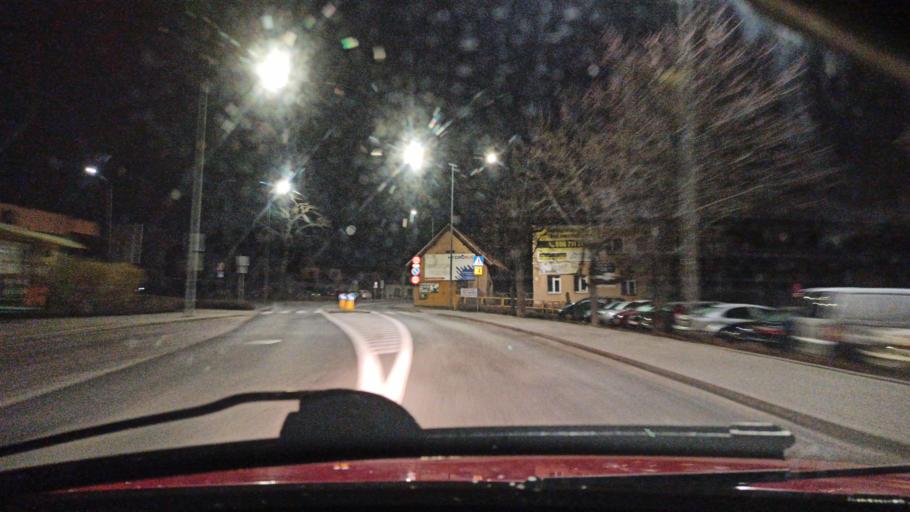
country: PL
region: Warmian-Masurian Voivodeship
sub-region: Powiat elblaski
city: Elblag
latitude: 54.1678
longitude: 19.4157
